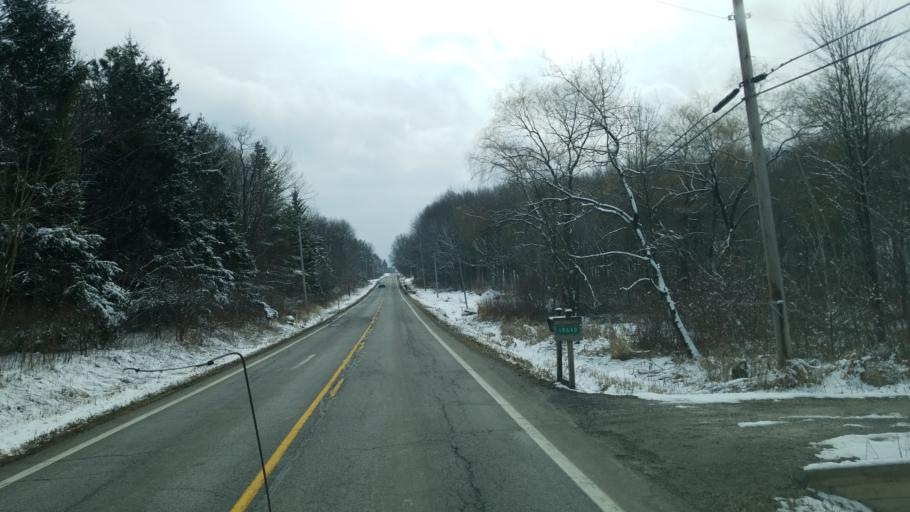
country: US
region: Ohio
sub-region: Portage County
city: Hiram
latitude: 41.3622
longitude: -81.1431
